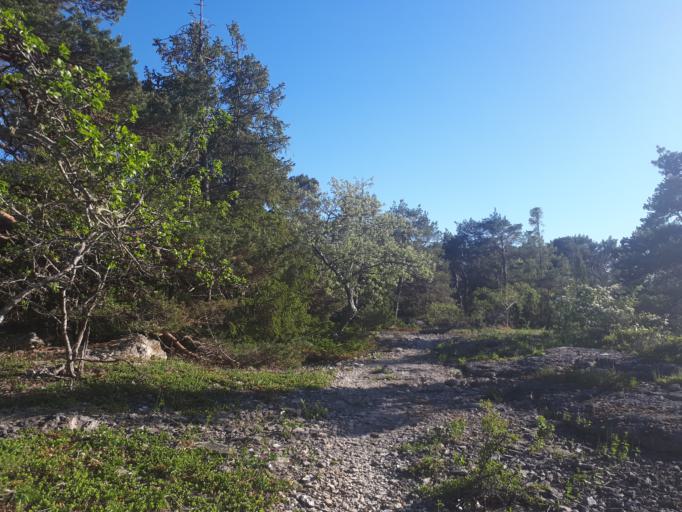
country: SE
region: Gotland
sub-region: Gotland
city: Vibble
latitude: 57.6120
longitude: 18.2498
